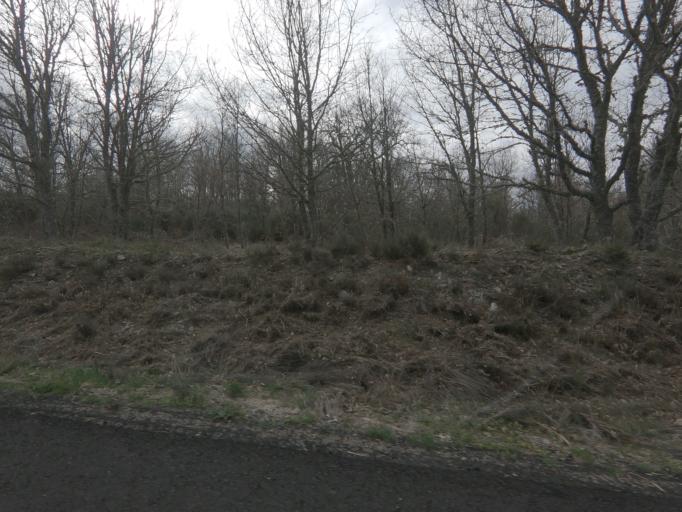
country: ES
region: Castille and Leon
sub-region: Provincia de Salamanca
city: Penaparda
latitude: 40.2779
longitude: -6.6782
